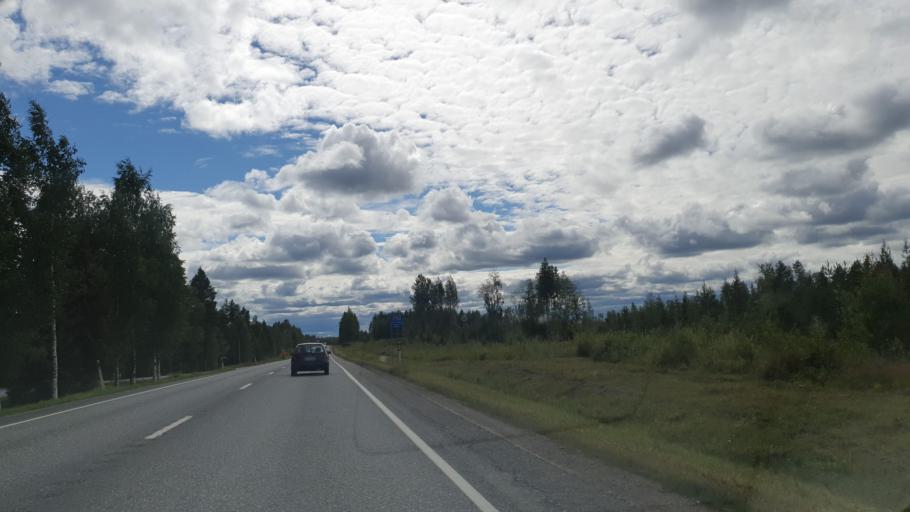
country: FI
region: Kainuu
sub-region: Kajaani
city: Kajaani
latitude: 64.1593
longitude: 27.5209
